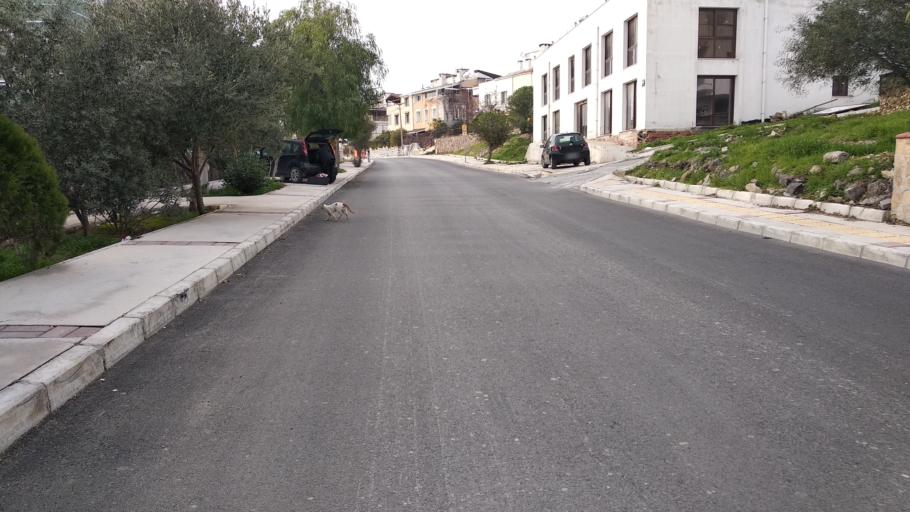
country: TR
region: Izmir
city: Karsiyaka
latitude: 38.4942
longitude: 27.0803
